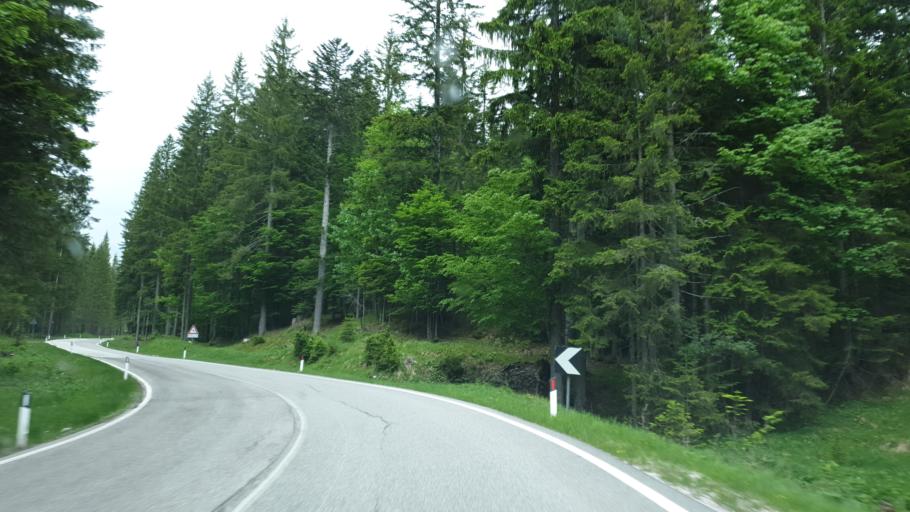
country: IT
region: Veneto
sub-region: Provincia di Belluno
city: San Vito
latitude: 46.5342
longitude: 12.2627
